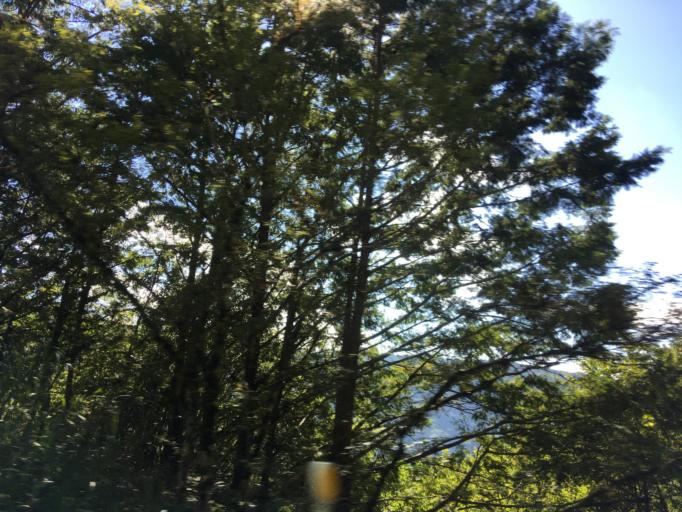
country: TW
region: Taiwan
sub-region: Yilan
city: Yilan
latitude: 24.5051
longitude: 121.5693
